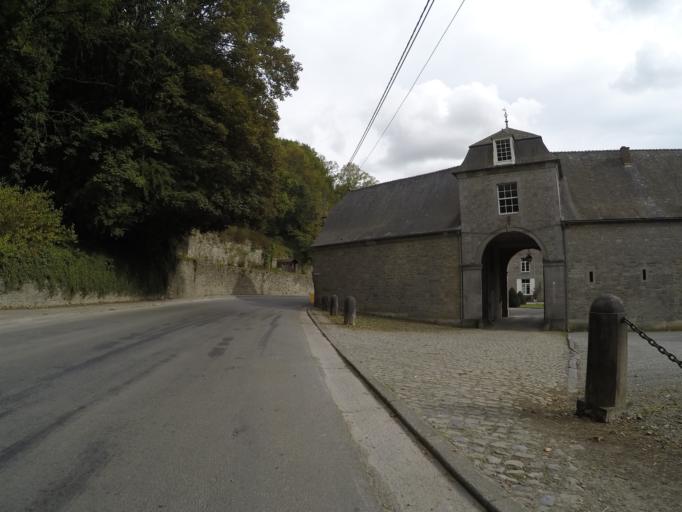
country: BE
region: Wallonia
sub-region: Province de Namur
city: Yvoir
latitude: 50.3274
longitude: 4.8863
